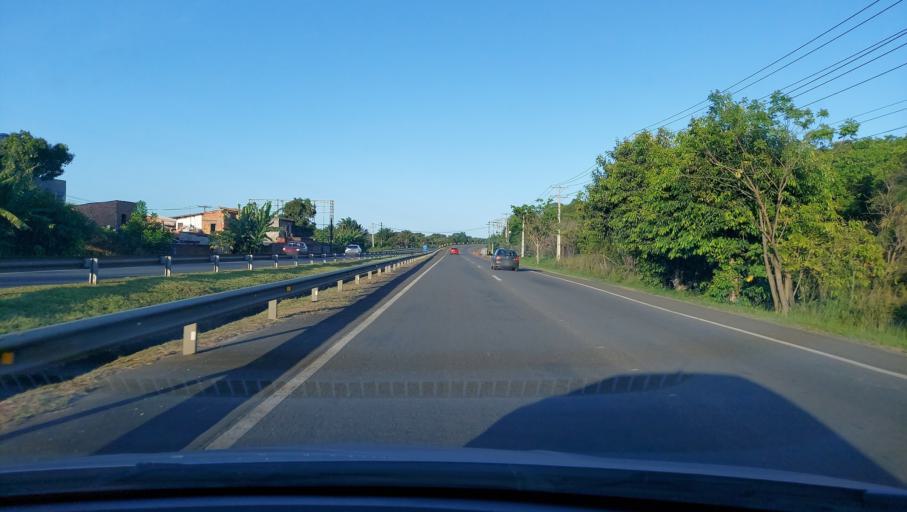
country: BR
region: Bahia
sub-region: Lauro De Freitas
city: Lauro de Freitas
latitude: -12.8024
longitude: -38.2248
